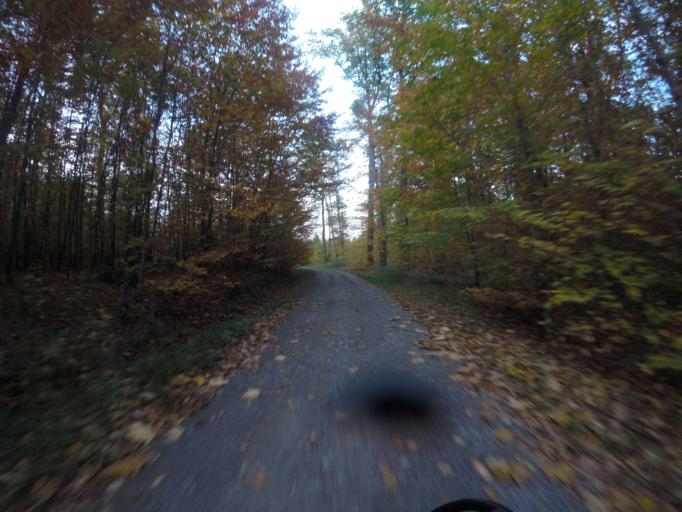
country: DE
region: Baden-Wuerttemberg
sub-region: Regierungsbezirk Stuttgart
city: Oberstenfeld
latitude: 48.9915
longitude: 9.3446
